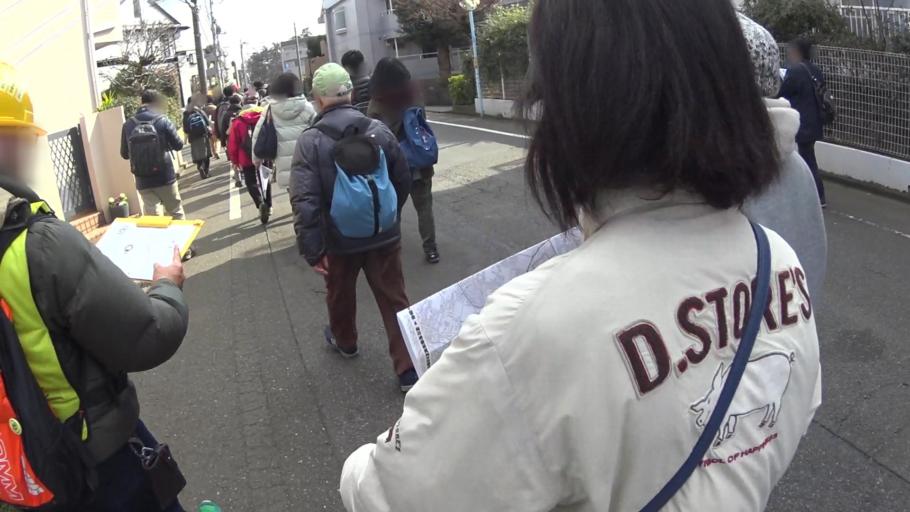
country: JP
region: Tokyo
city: Mitaka-shi
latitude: 35.6868
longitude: 139.5907
